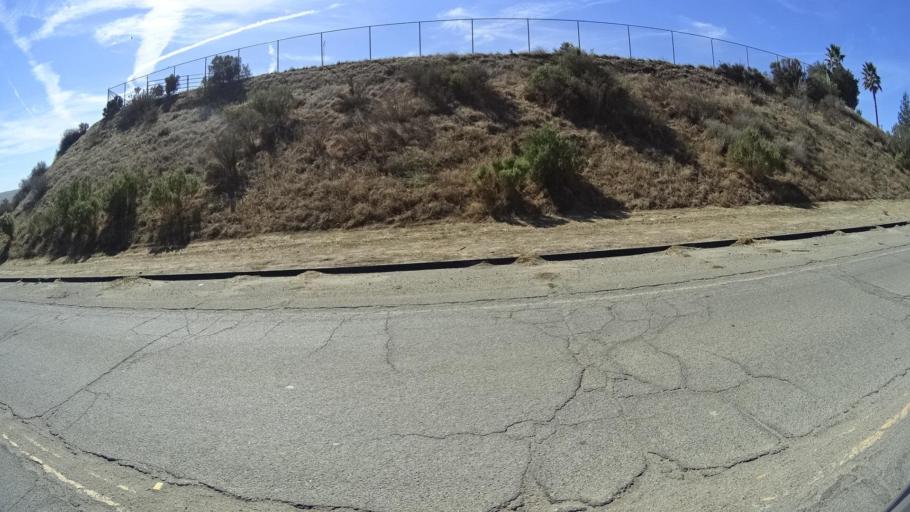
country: US
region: California
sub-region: Monterey County
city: King City
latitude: 36.0137
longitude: -120.9204
